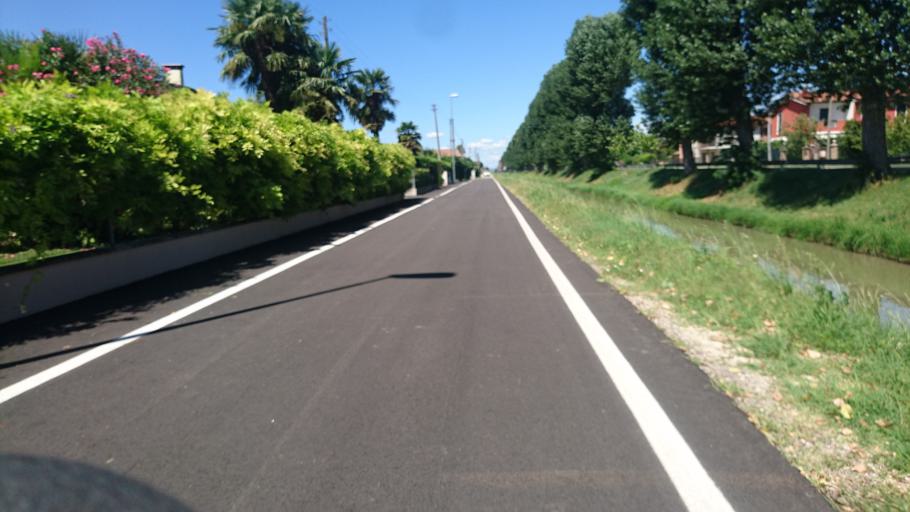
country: IT
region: Veneto
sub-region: Provincia di Padova
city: Sant'Angelo di Piove di Sacco
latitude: 45.3031
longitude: 12.0119
